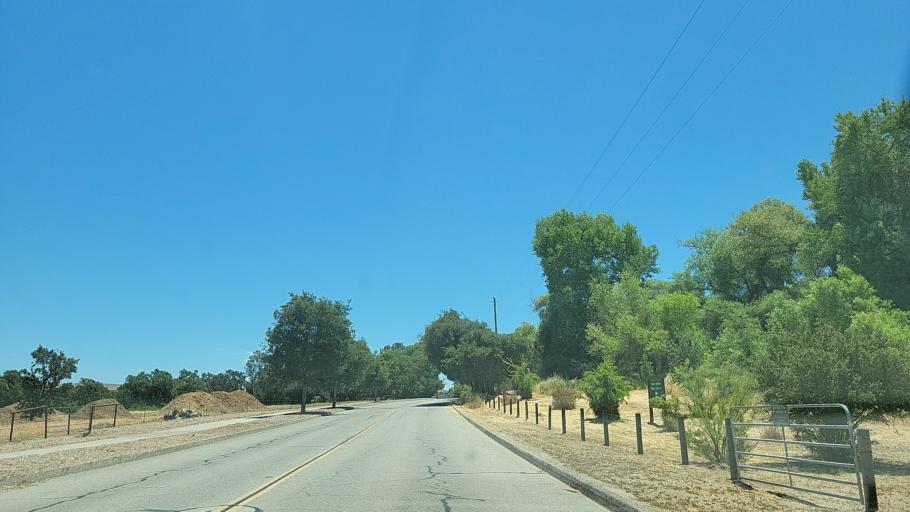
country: US
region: California
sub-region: San Luis Obispo County
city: Atascadero
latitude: 35.5135
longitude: -120.6769
